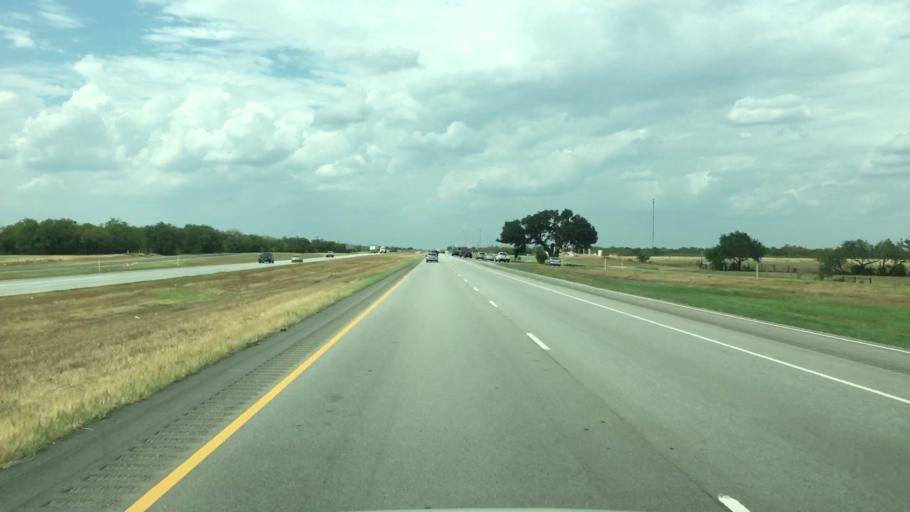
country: US
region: Texas
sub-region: Live Oak County
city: Three Rivers
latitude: 28.5321
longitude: -98.1881
